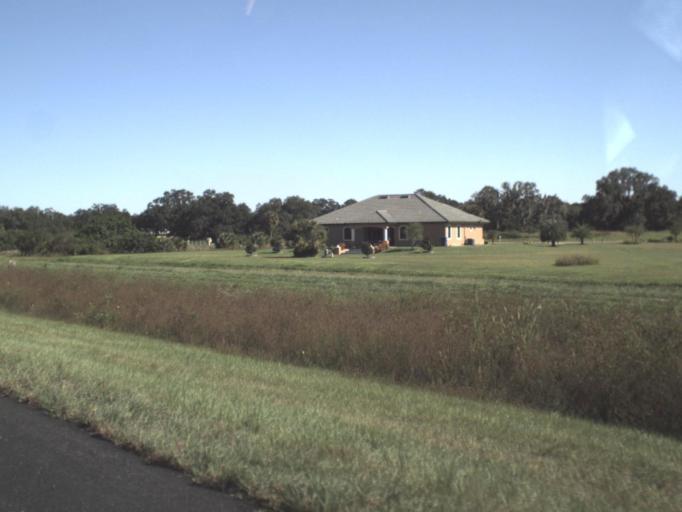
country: US
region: Florida
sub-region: Hendry County
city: Port LaBelle
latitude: 26.7633
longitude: -81.3950
